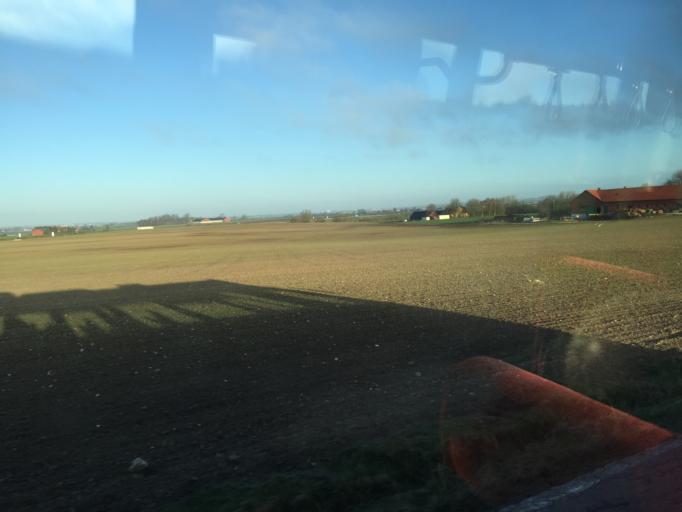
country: SE
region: Skane
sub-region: Lunds Kommun
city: Genarp
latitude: 55.6557
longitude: 13.3479
